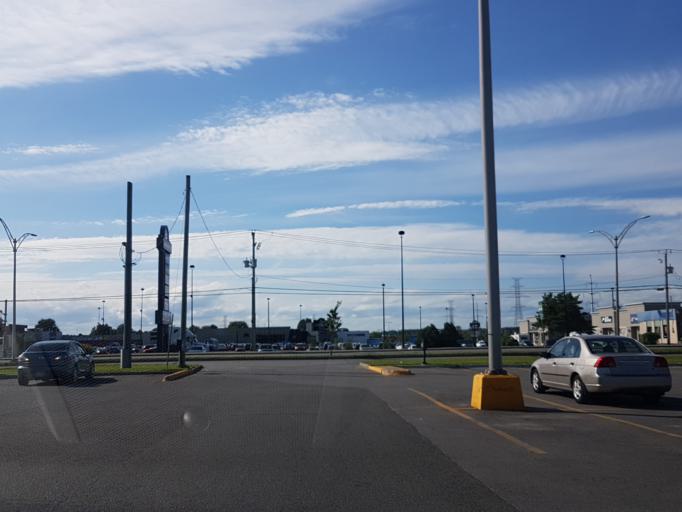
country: CA
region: Quebec
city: Sainte-Catherine
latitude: 46.3243
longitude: -72.5637
